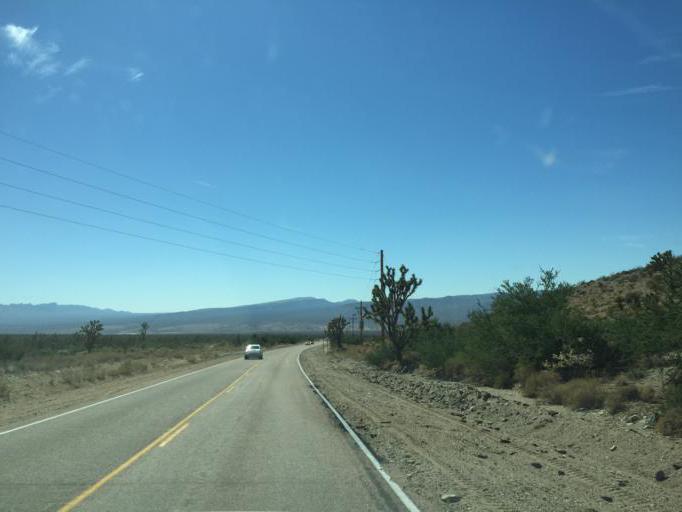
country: US
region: Arizona
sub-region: Mohave County
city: Meadview
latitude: 35.8506
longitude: -114.0854
